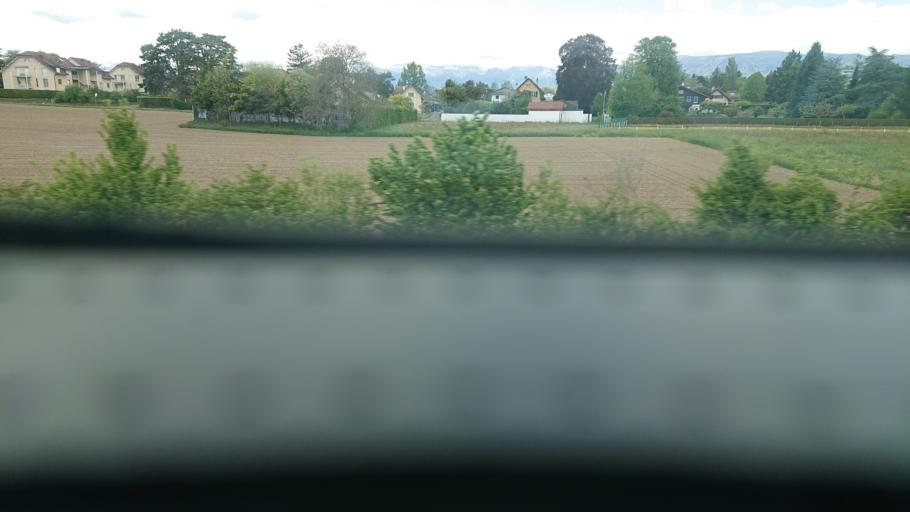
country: CH
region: Vaud
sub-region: Nyon District
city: Coppet
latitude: 46.3165
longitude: 6.1873
